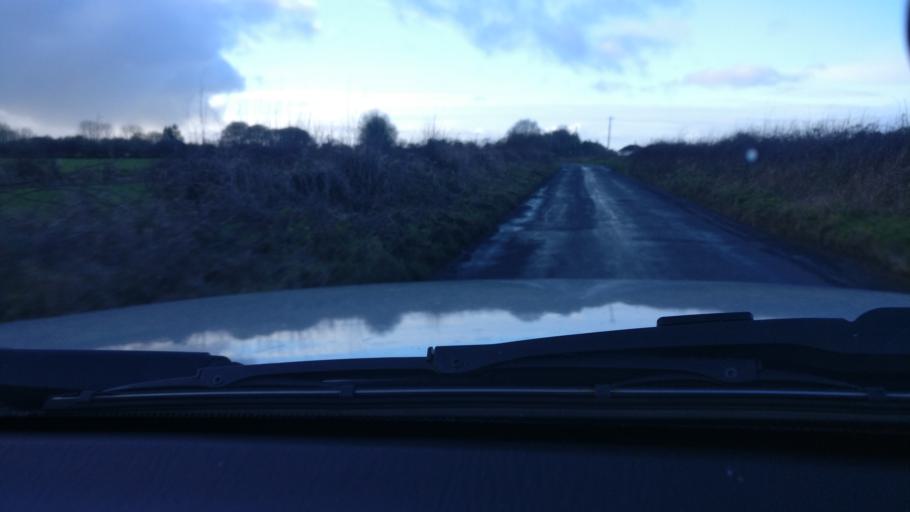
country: IE
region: Connaught
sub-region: County Galway
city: Ballinasloe
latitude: 53.2230
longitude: -8.3737
